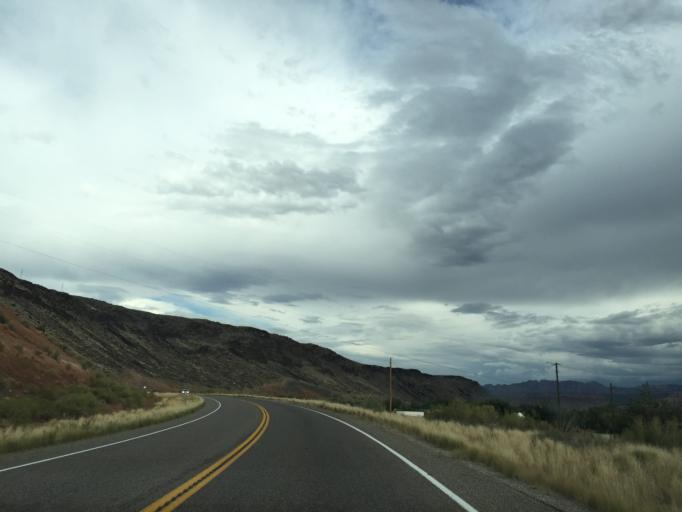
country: US
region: Utah
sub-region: Washington County
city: LaVerkin
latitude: 37.1953
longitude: -113.1542
